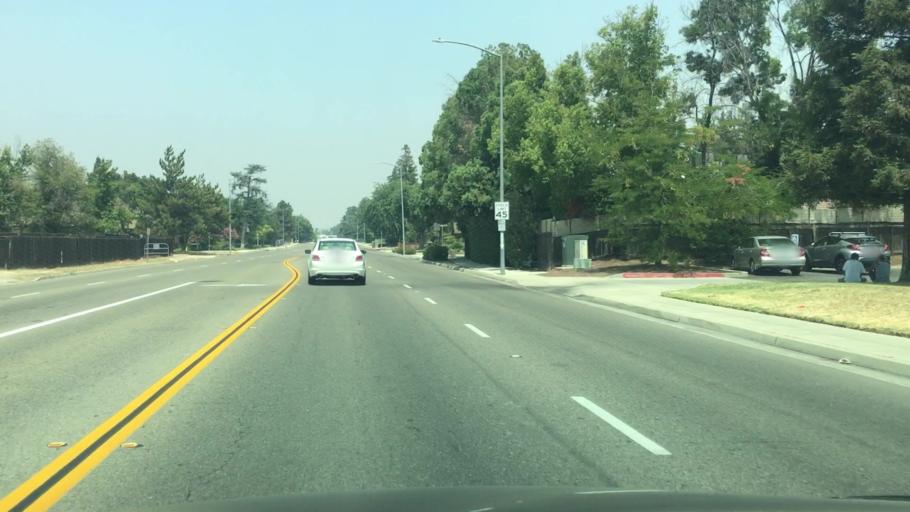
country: US
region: California
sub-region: Fresno County
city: Clovis
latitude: 36.8306
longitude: -119.7134
